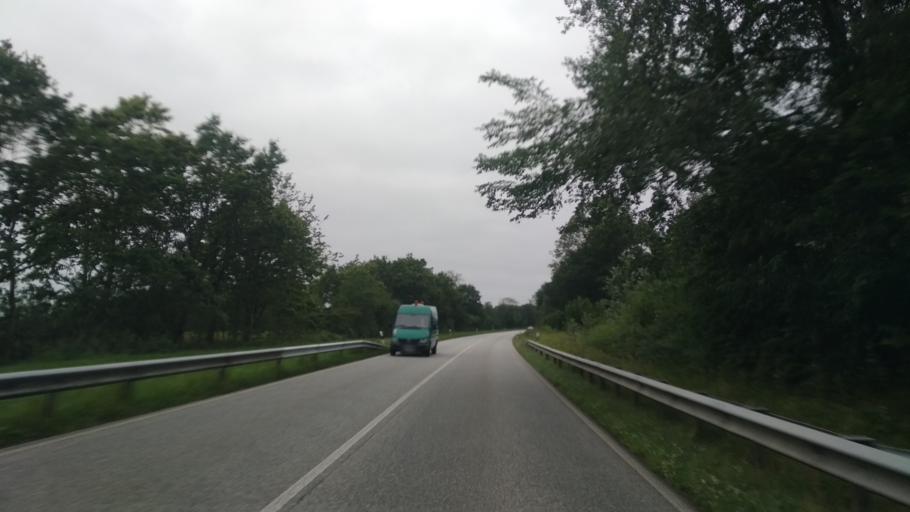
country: DE
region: Schleswig-Holstein
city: Sieverstedt
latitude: 54.6478
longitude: 9.4505
